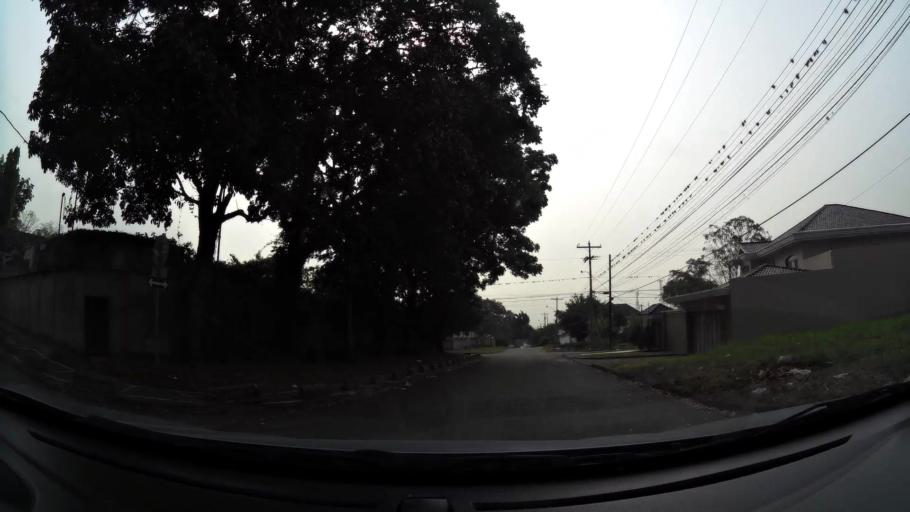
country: HN
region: Cortes
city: Armenta
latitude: 15.5012
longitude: -88.0479
